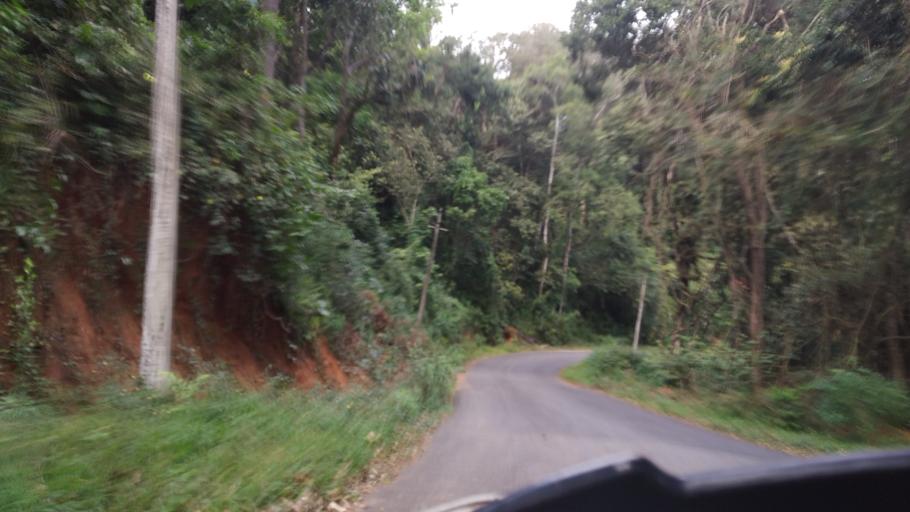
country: IN
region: Karnataka
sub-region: Kodagu
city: Ponnampet
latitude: 12.0315
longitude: 75.9248
